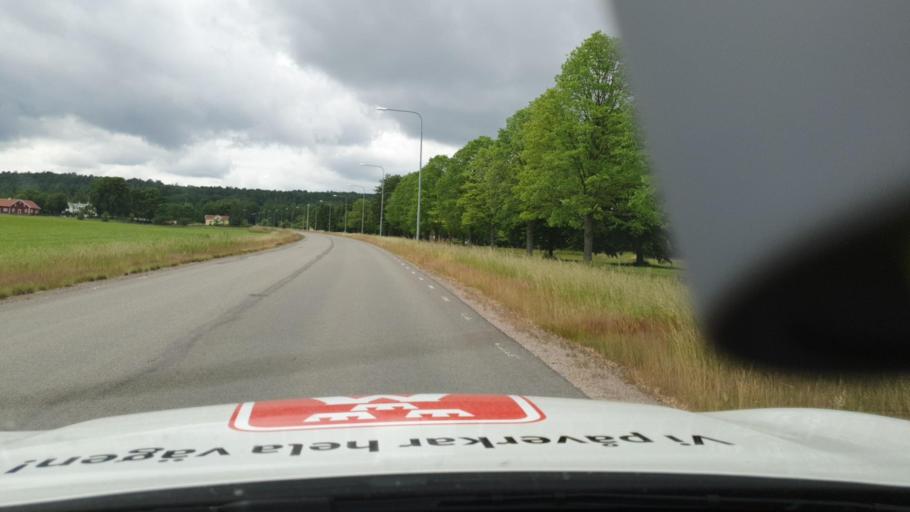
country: SE
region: Vaestra Goetaland
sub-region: Hjo Kommun
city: Hjo
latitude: 58.2907
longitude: 14.2727
